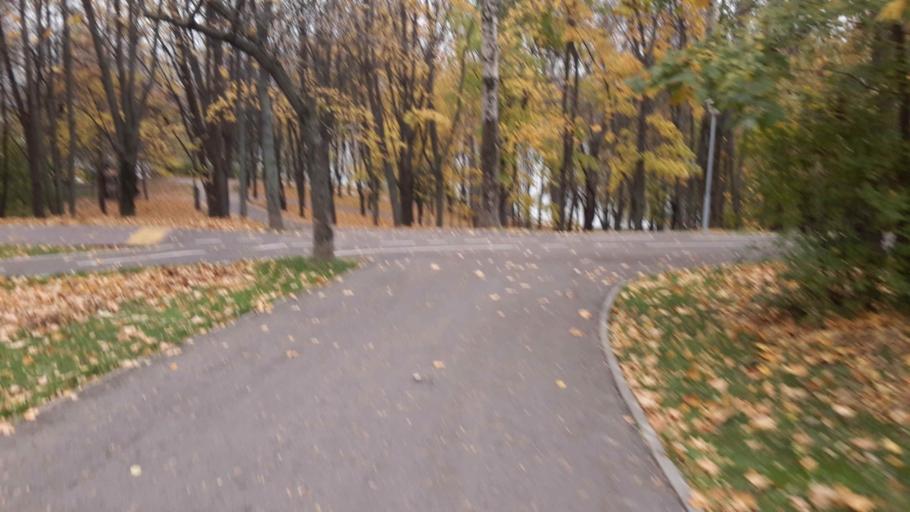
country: RU
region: Moscow
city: Mar'ino
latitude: 55.6337
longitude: 37.7089
